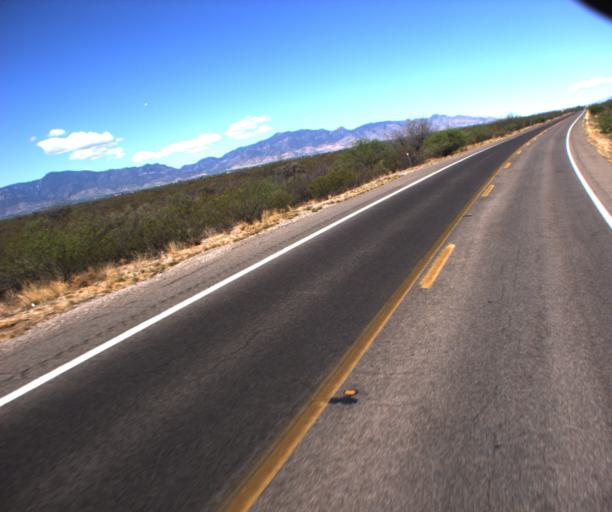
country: US
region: Arizona
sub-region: Cochise County
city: Sierra Vista Southeast
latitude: 31.5463
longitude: -110.1580
